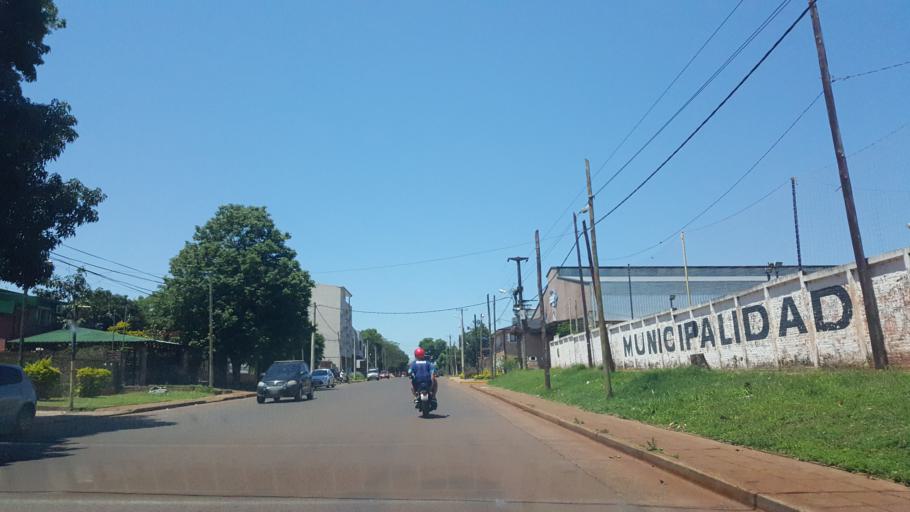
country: AR
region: Misiones
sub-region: Departamento de Capital
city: Posadas
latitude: -27.3824
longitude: -55.9177
